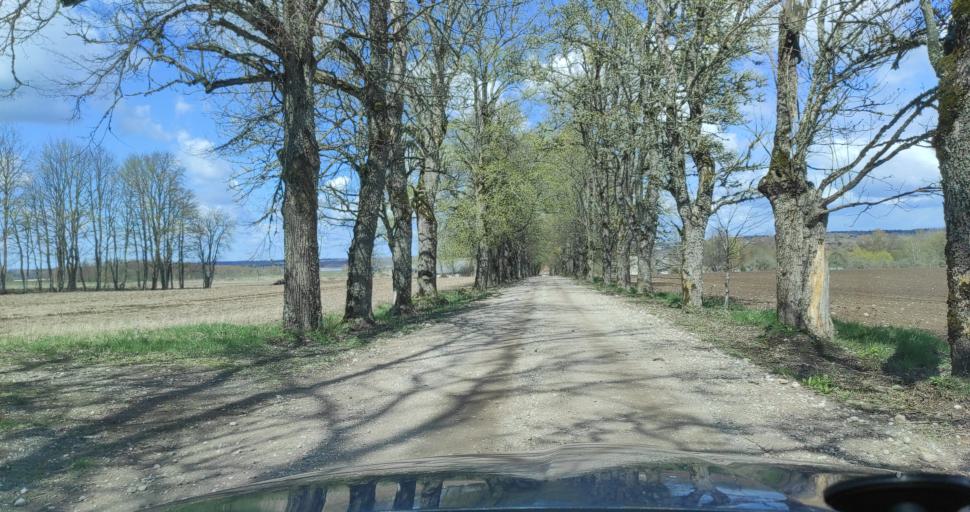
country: LV
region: Kuldigas Rajons
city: Kuldiga
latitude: 56.8599
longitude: 21.8134
